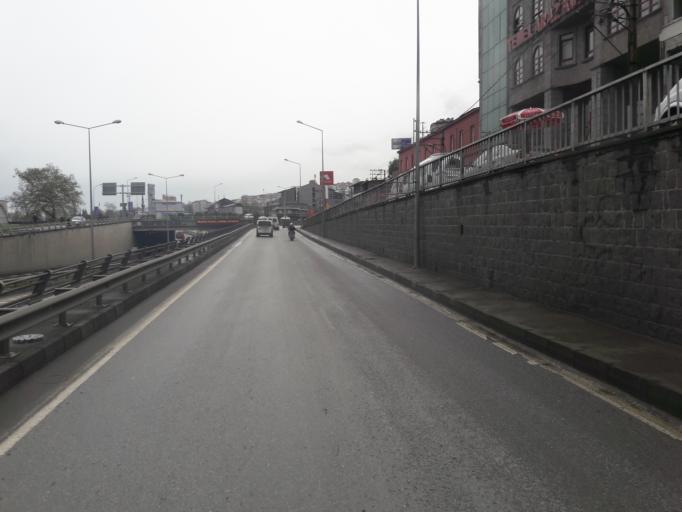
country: TR
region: Trabzon
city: Trabzon
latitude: 41.0004
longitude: 39.7417
